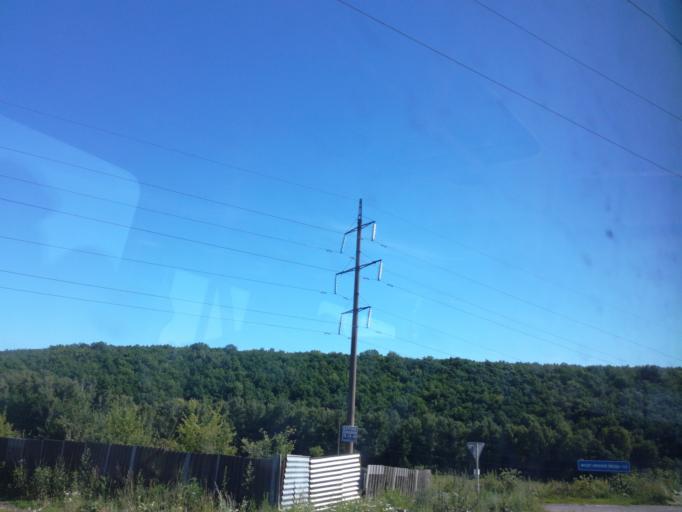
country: RU
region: Kursk
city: Kursk
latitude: 51.7944
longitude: 36.1935
